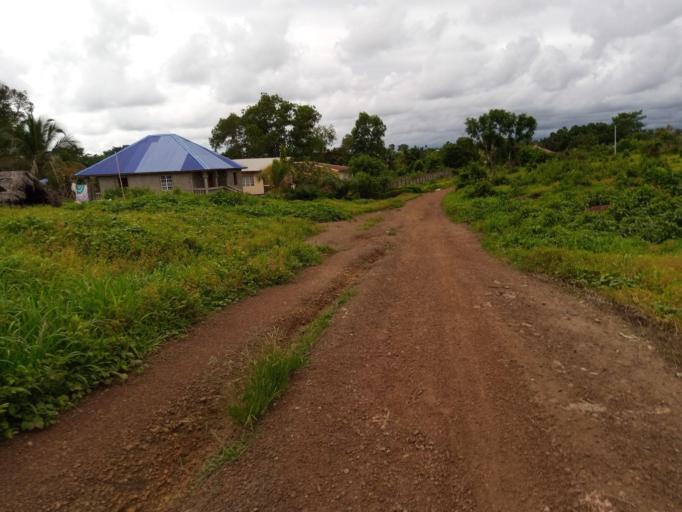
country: SL
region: Southern Province
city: Moyamba
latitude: 8.1674
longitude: -12.4261
